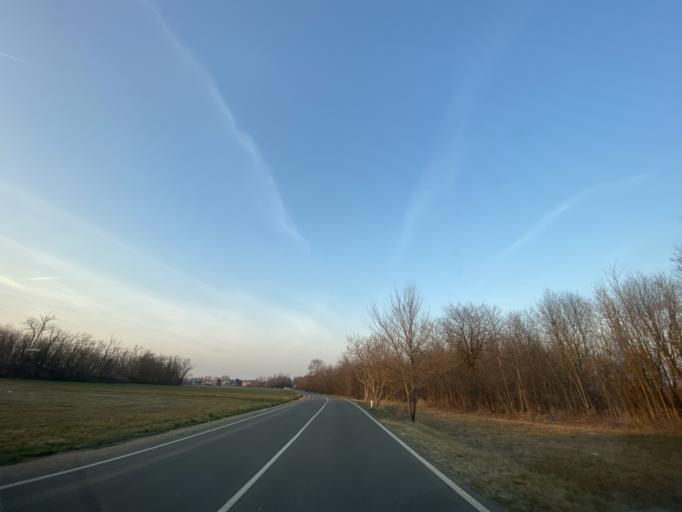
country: IT
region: Lombardy
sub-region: Citta metropolitana di Milano
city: Garbagnate Milanese
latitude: 45.5821
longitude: 9.0629
